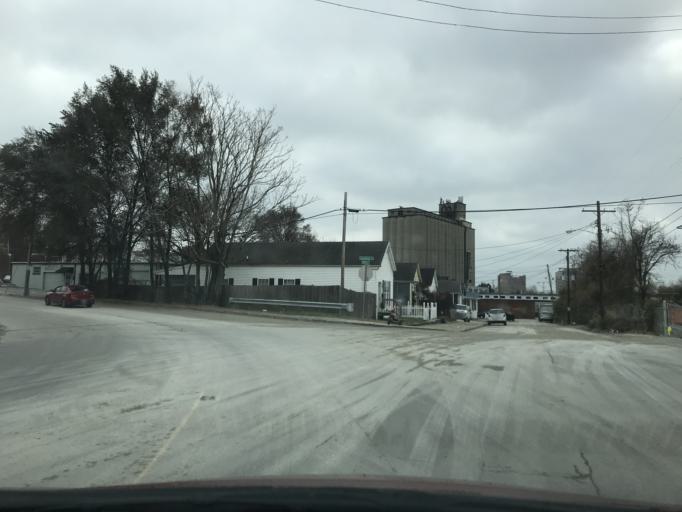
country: US
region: Kentucky
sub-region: Jefferson County
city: Louisville
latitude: 38.2477
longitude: -85.7316
